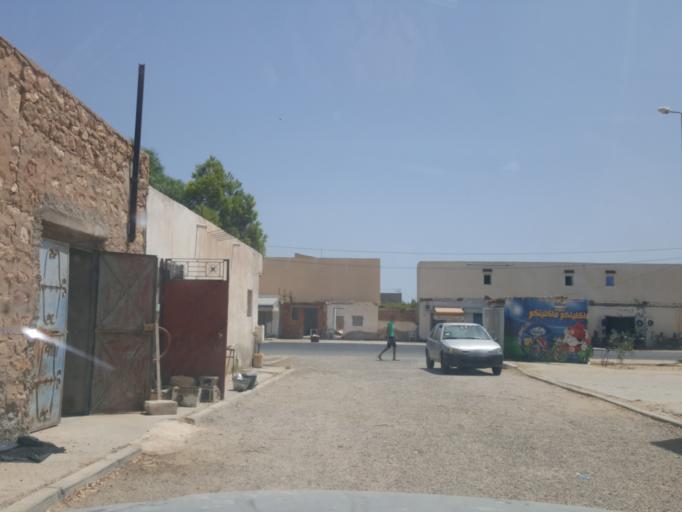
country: TN
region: Safaqis
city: Skhira
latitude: 34.1043
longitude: 9.9828
